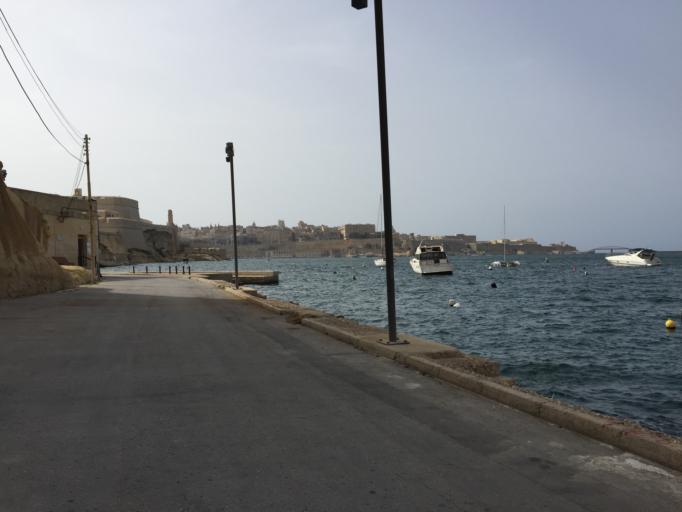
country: MT
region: Il-Birgu
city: Vittoriosa
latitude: 35.8895
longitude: 14.5222
